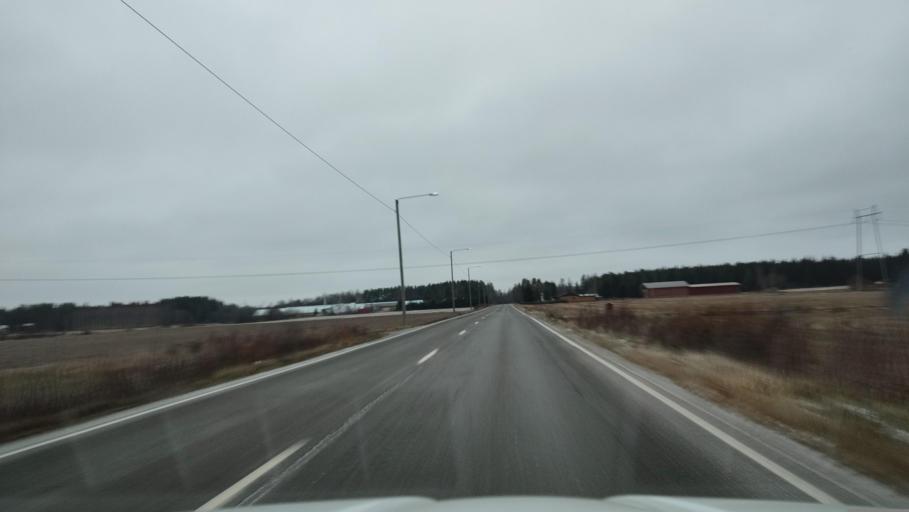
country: FI
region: Southern Ostrobothnia
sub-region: Suupohja
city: Karijoki
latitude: 62.2370
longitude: 21.6110
